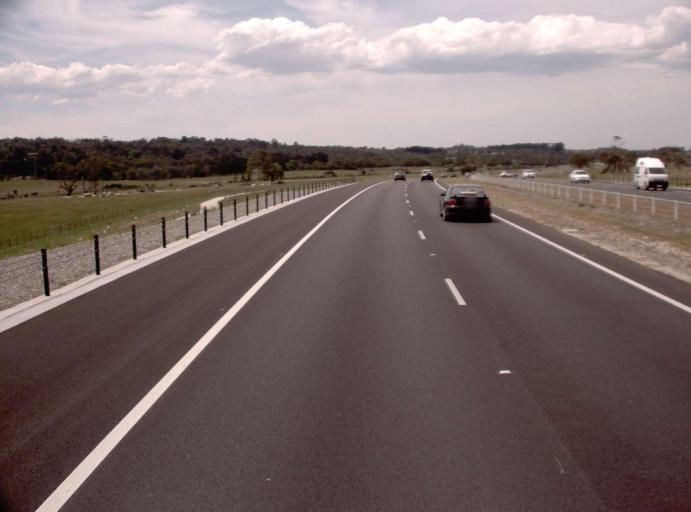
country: AU
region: Victoria
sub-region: Mornington Peninsula
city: Moorooduc
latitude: -38.2083
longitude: 145.1316
